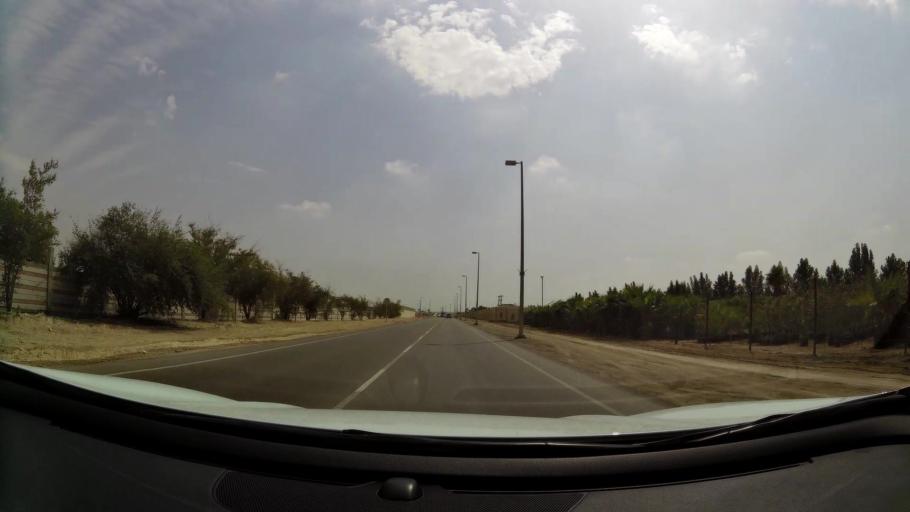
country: AE
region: Abu Dhabi
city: Abu Dhabi
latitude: 24.5168
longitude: 54.6564
